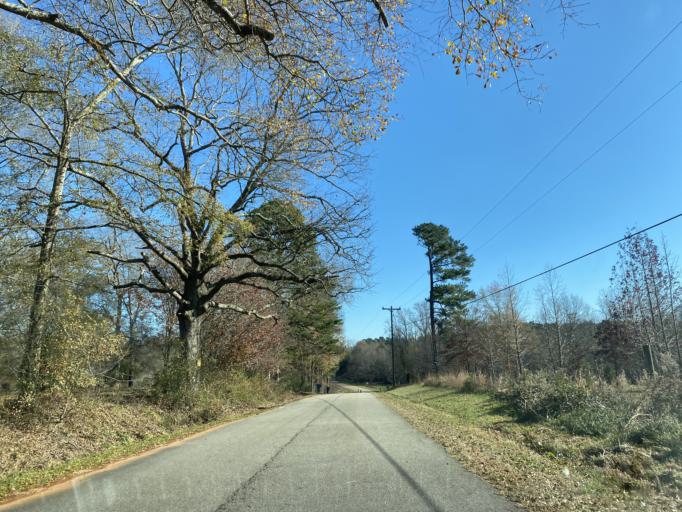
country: US
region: South Carolina
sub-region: Spartanburg County
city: Mayo
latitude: 35.1466
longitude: -81.7845
